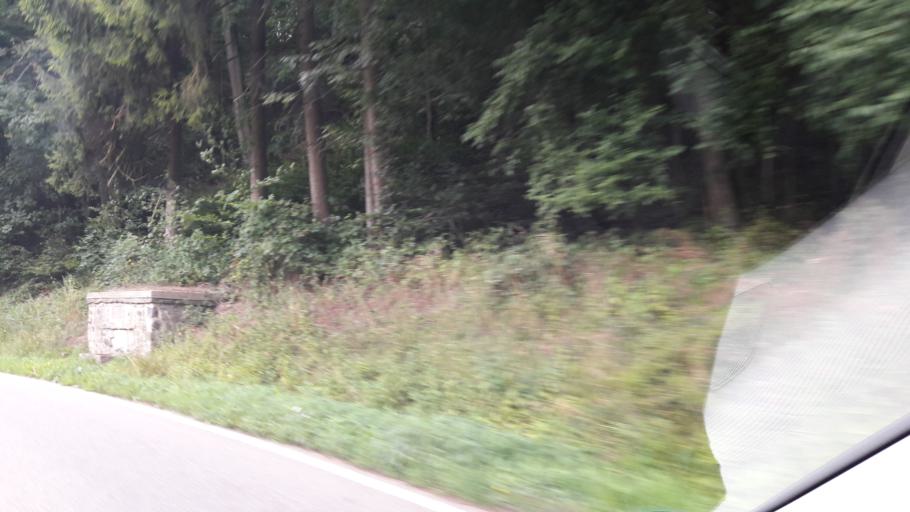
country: DE
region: Saarland
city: Tholey
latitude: 49.4835
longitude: 6.9907
